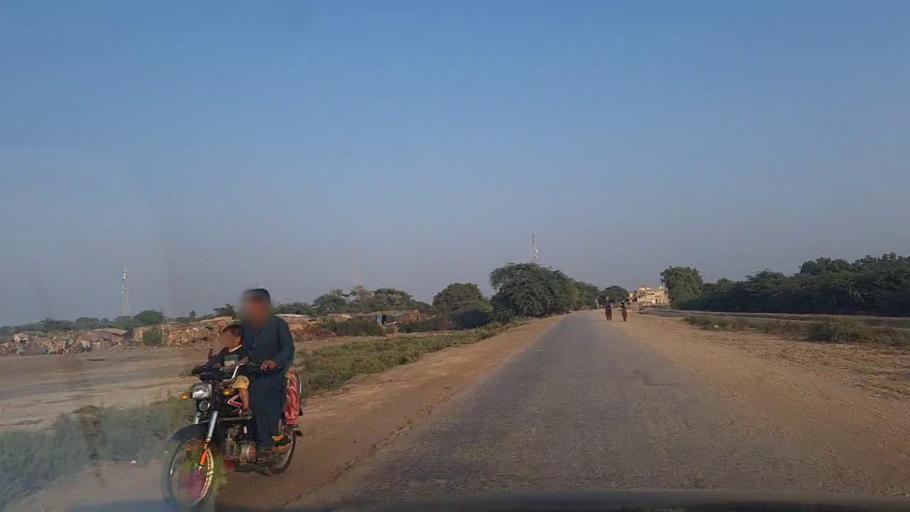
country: PK
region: Sindh
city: Keti Bandar
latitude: 24.3010
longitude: 67.5999
